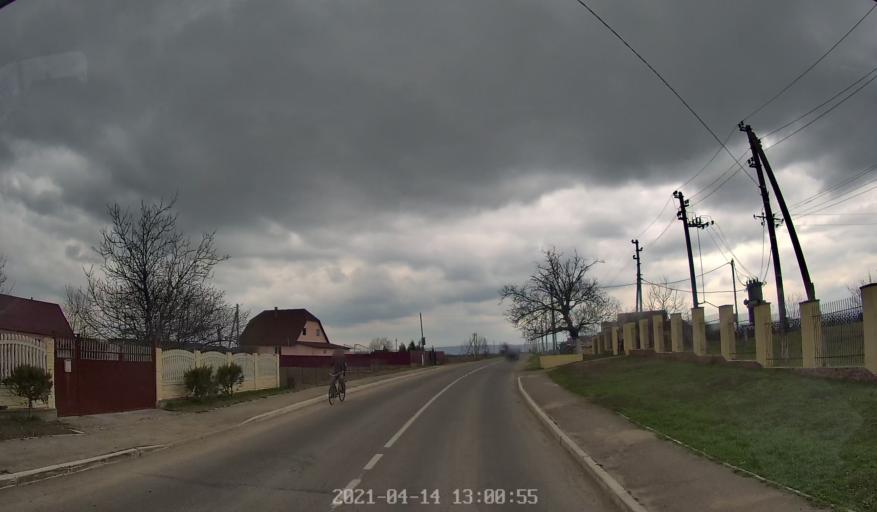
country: MD
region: Chisinau
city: Vadul lui Voda
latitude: 47.1355
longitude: 29.1190
